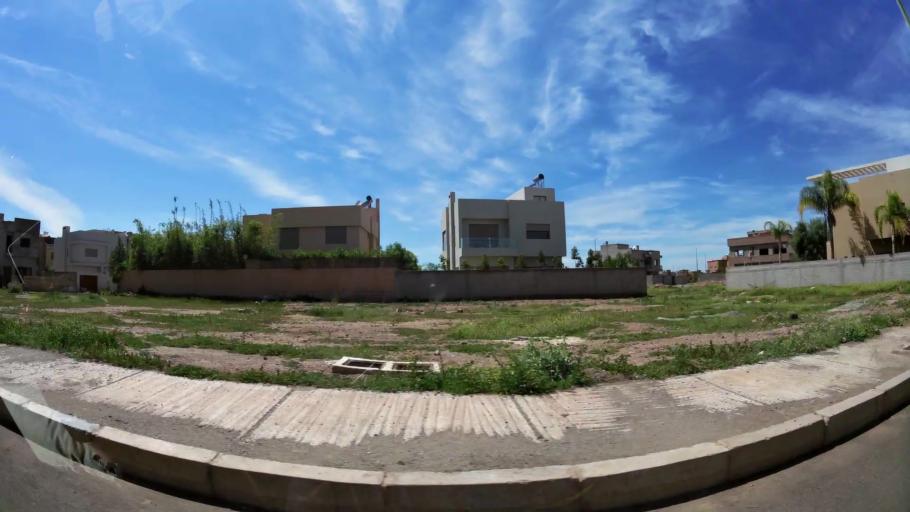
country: MA
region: Marrakech-Tensift-Al Haouz
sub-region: Marrakech
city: Marrakesh
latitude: 31.6519
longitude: -8.0728
